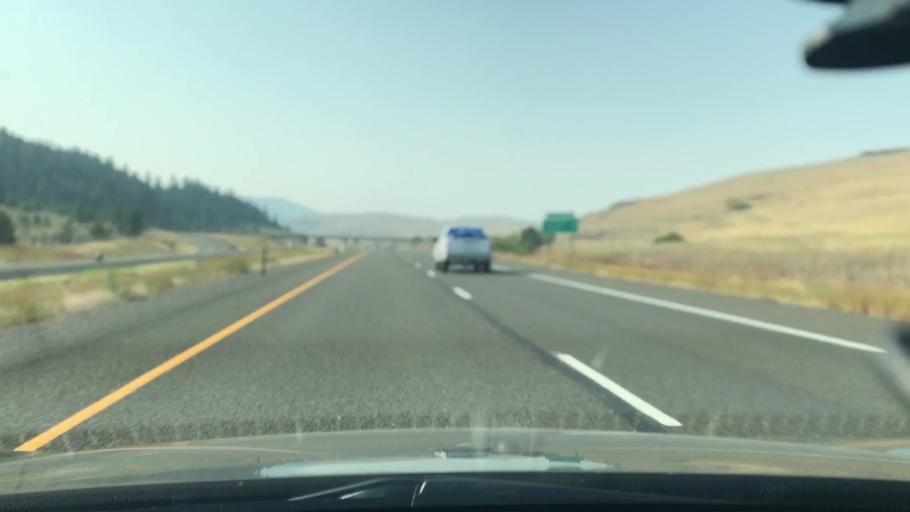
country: US
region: Oregon
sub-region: Union County
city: Union
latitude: 45.1794
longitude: -117.9832
